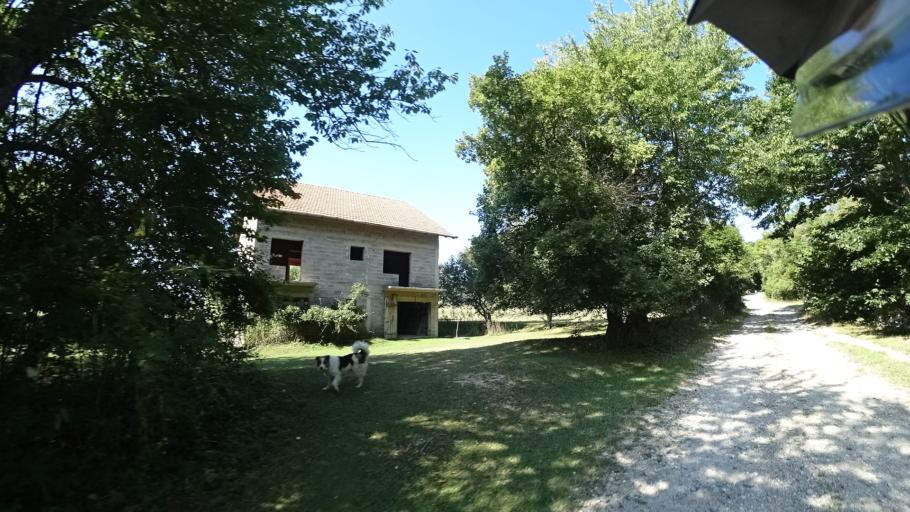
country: HR
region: Zadarska
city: Gracac
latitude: 44.2938
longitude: 16.0553
